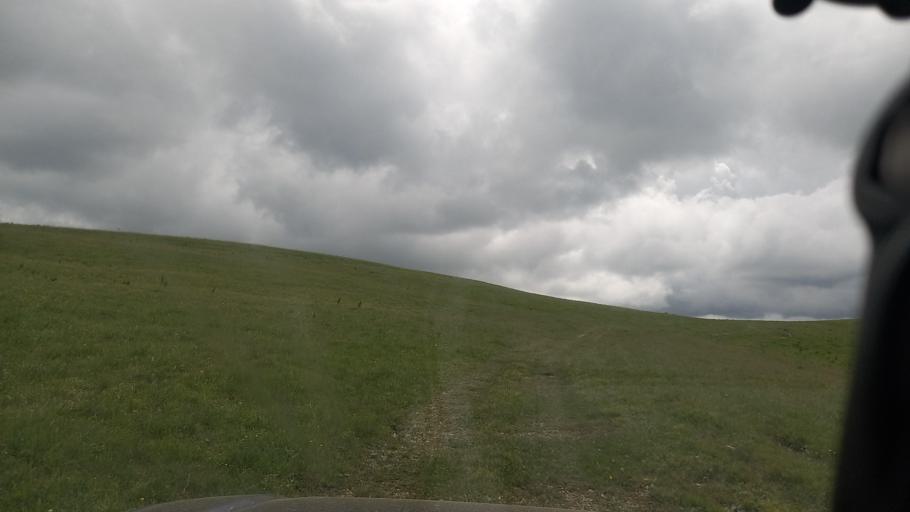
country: RU
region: Karachayevo-Cherkesiya
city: Pregradnaya
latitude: 43.9917
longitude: 41.2854
